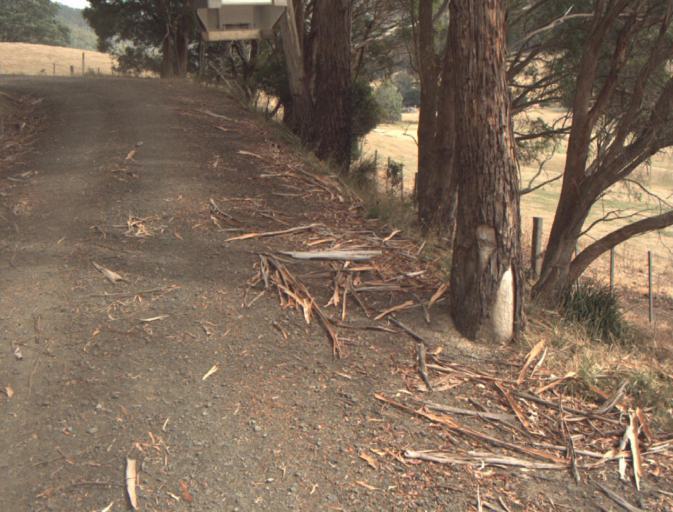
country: AU
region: Tasmania
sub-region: Dorset
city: Scottsdale
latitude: -41.4552
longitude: 147.5984
